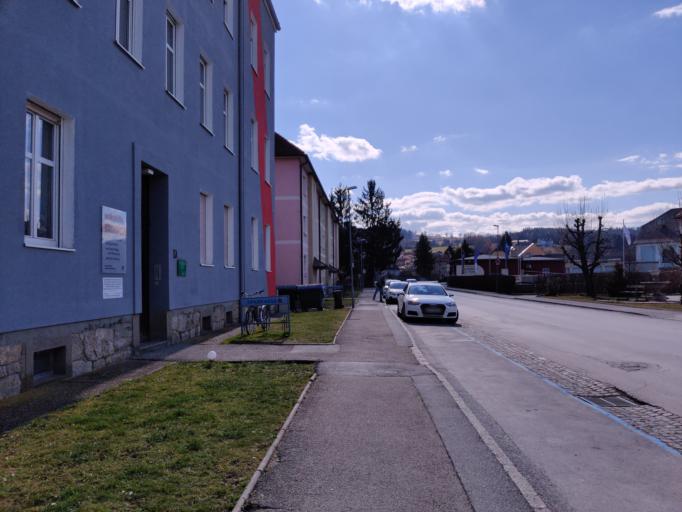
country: AT
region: Styria
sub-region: Politischer Bezirk Voitsberg
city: Voitsberg
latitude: 47.0470
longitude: 15.1485
